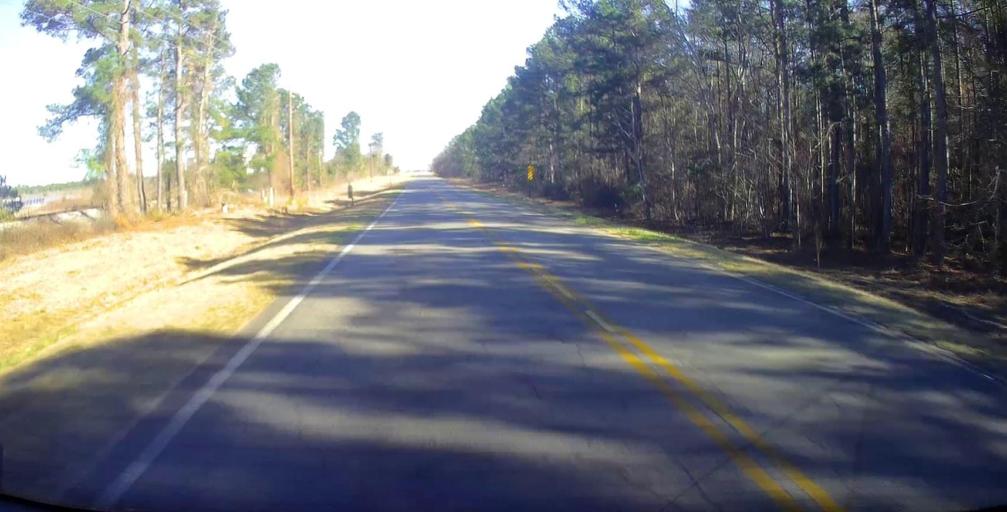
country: US
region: Georgia
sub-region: Taylor County
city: Butler
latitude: 32.5664
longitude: -84.2683
